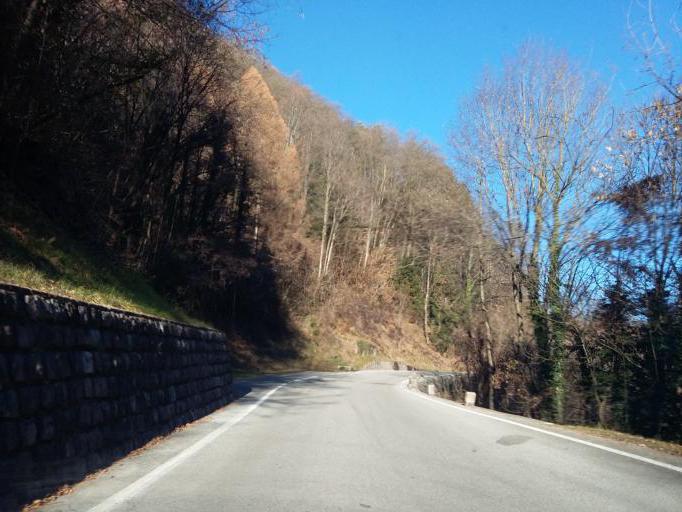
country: IT
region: Trentino-Alto Adige
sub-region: Provincia di Trento
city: Brione
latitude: 45.8928
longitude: 10.5991
